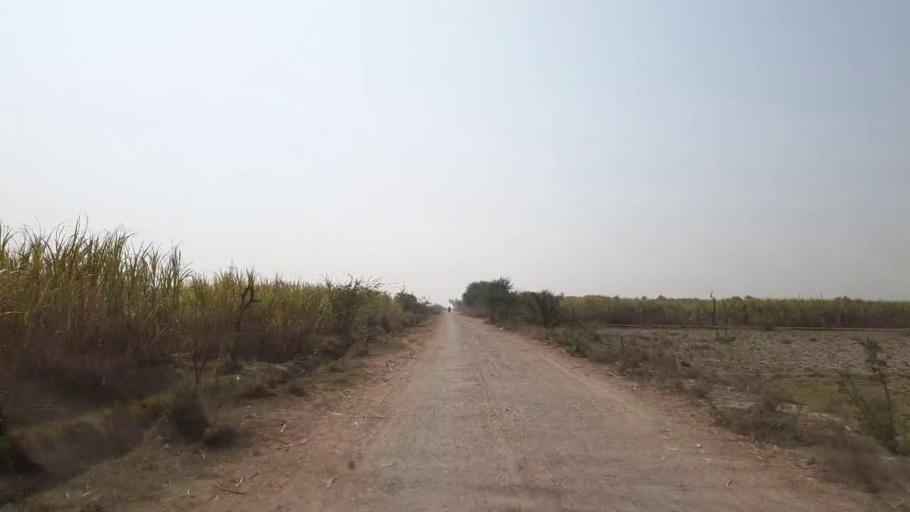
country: PK
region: Sindh
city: Mirpur Khas
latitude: 25.5996
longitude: 69.0248
